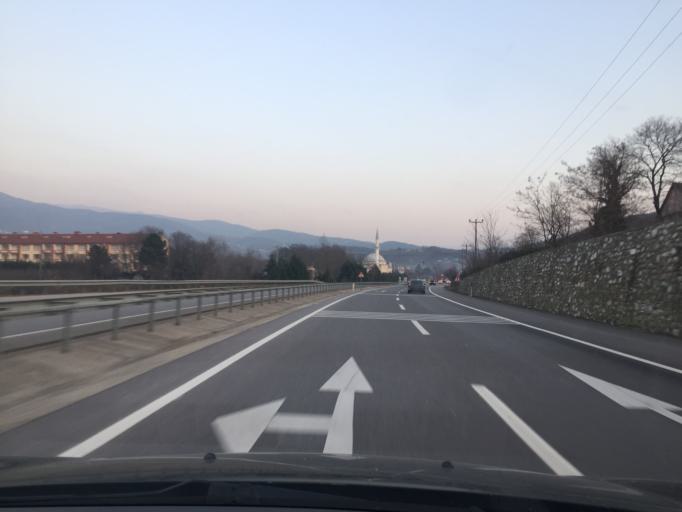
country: TR
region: Sakarya
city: Akyazi
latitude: 40.6257
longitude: 30.6486
